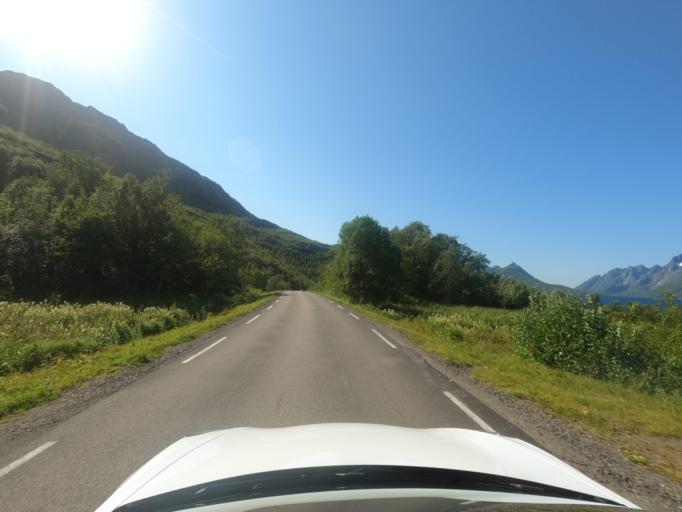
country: NO
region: Nordland
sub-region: Hadsel
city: Stokmarknes
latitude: 68.3299
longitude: 15.0158
